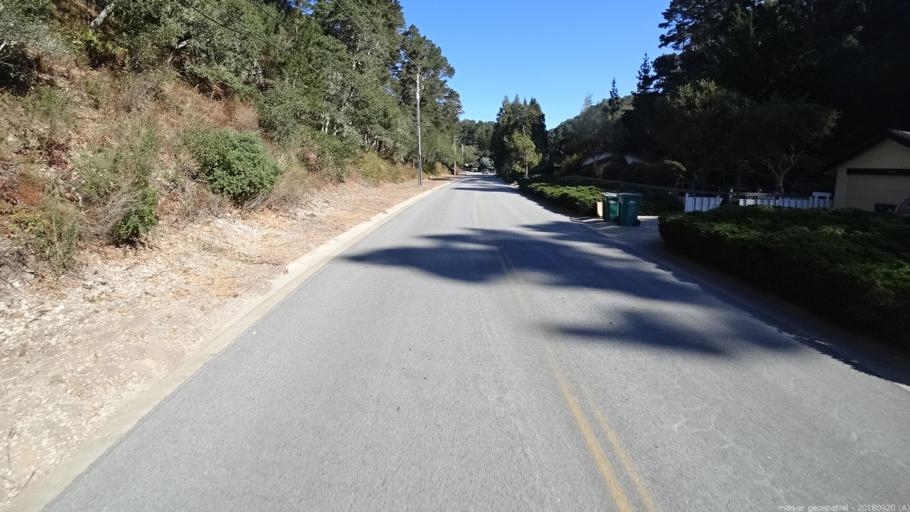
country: US
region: California
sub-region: Monterey County
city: Carmel-by-the-Sea
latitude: 36.5503
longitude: -121.8962
